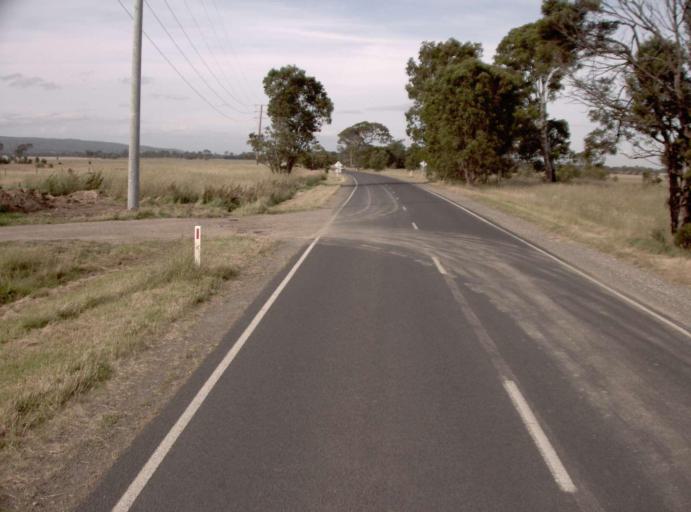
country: AU
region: Victoria
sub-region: Latrobe
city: Traralgon
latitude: -38.0969
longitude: 146.5970
